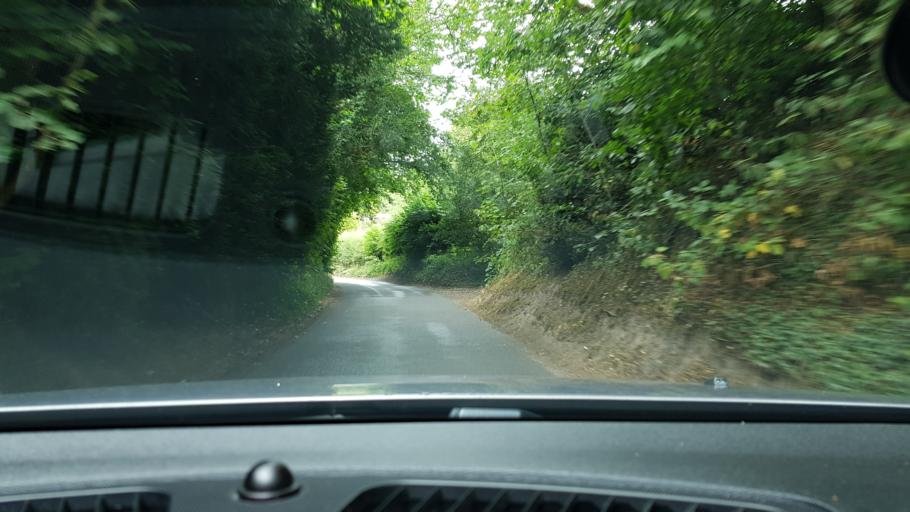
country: GB
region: England
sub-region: Wiltshire
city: Shalbourne
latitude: 51.3640
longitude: -1.5263
